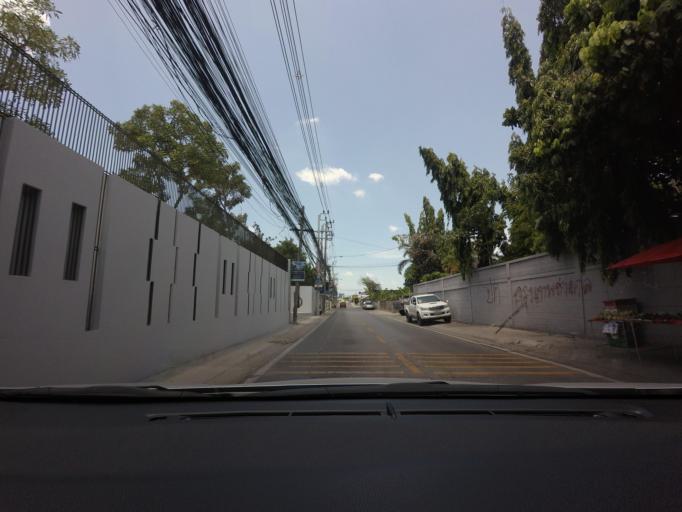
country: TH
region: Bangkok
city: Phra Khanong
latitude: 13.7255
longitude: 100.6160
